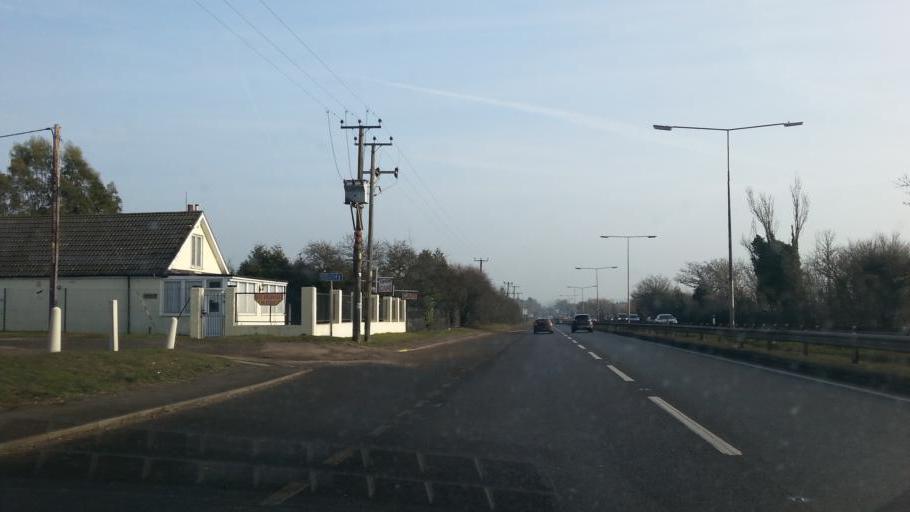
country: GB
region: England
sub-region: Essex
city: Wickford
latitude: 51.5902
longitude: 0.5273
